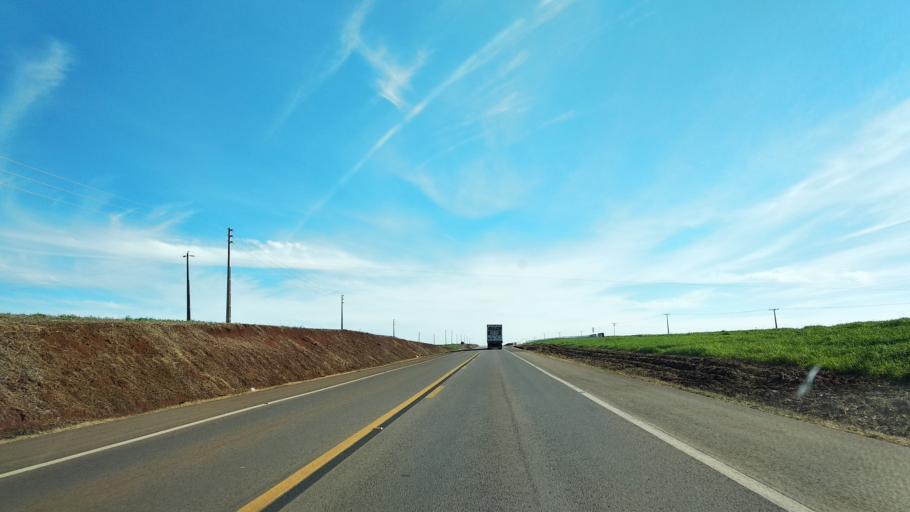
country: BR
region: Santa Catarina
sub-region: Campos Novos
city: Campos Novos
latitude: -27.4863
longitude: -51.3184
